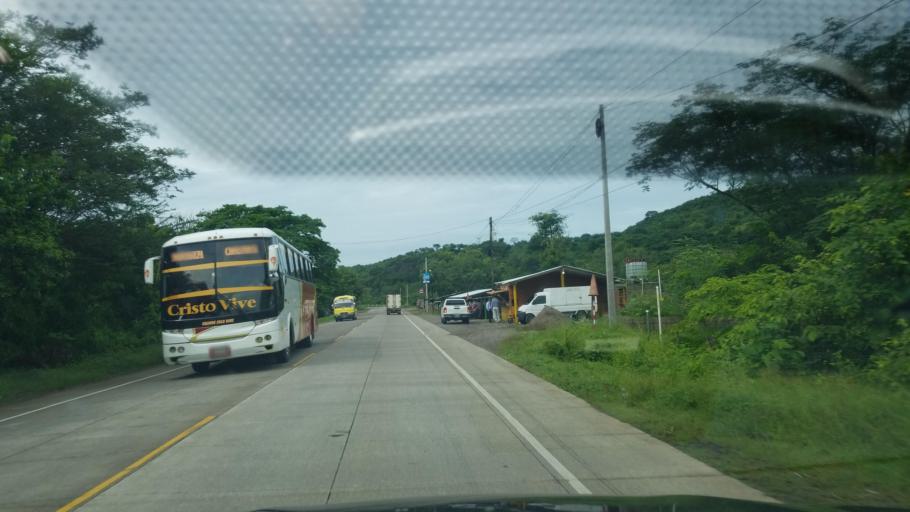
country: HN
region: Choluteca
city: Pespire
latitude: 13.6254
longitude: -87.3733
